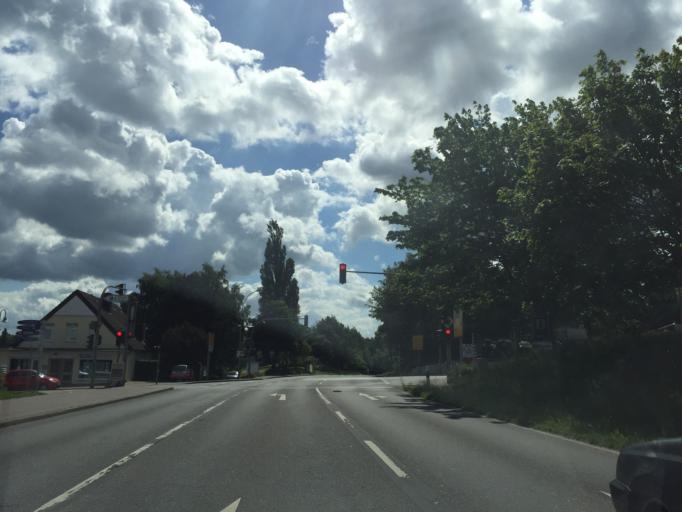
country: DE
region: Schleswig-Holstein
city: Scharbeutz
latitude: 54.0228
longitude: 10.7498
